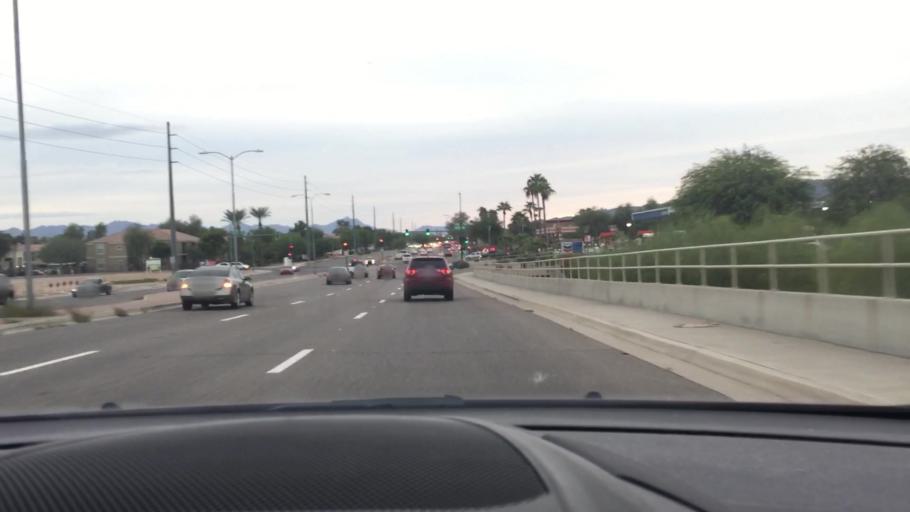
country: US
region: Arizona
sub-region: Maricopa County
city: Guadalupe
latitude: 33.3055
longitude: -111.9742
